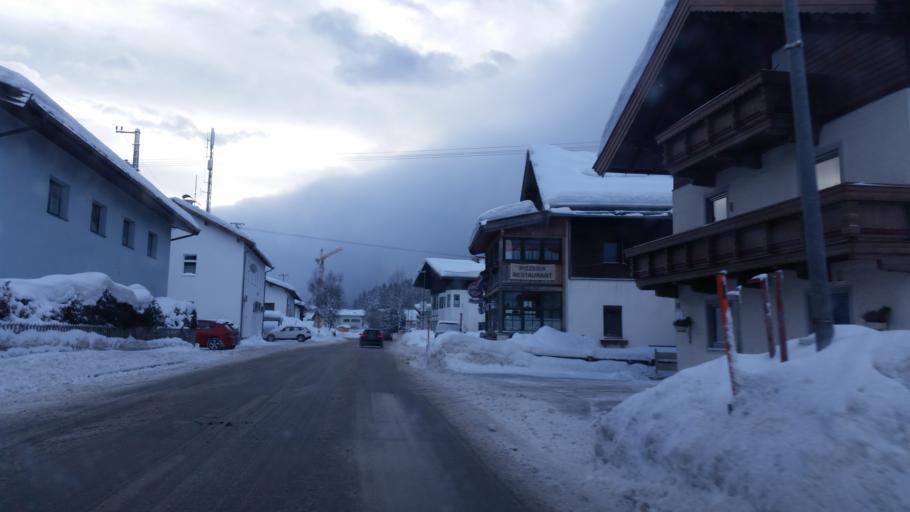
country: AT
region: Tyrol
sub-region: Politischer Bezirk Kitzbuhel
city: Hochfilzen
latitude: 47.4678
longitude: 12.6255
